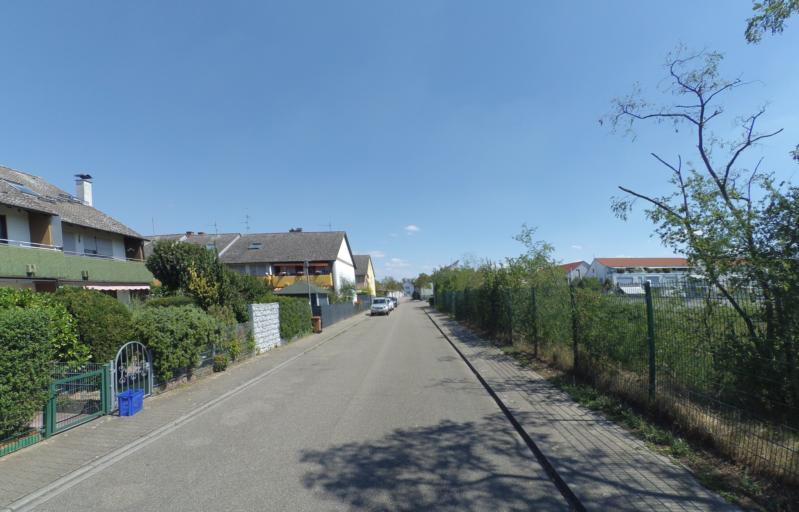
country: DE
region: Baden-Wuerttemberg
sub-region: Karlsruhe Region
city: Bruhl
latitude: 49.4073
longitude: 8.5344
